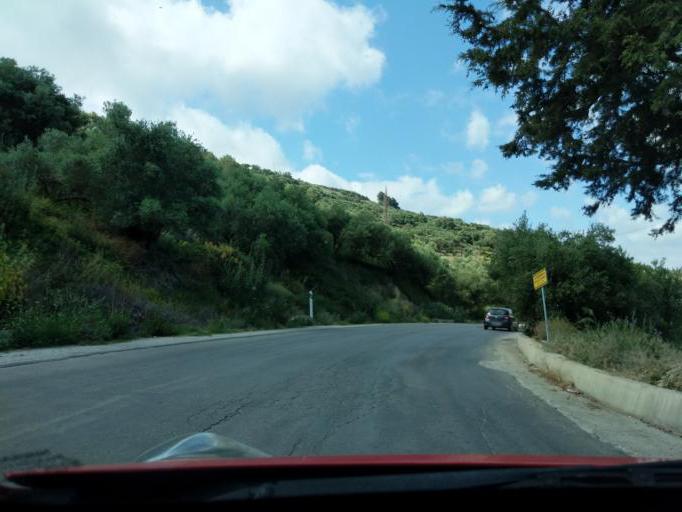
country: GR
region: Crete
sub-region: Nomos Chanias
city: Kissamos
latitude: 35.4330
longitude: 23.6858
